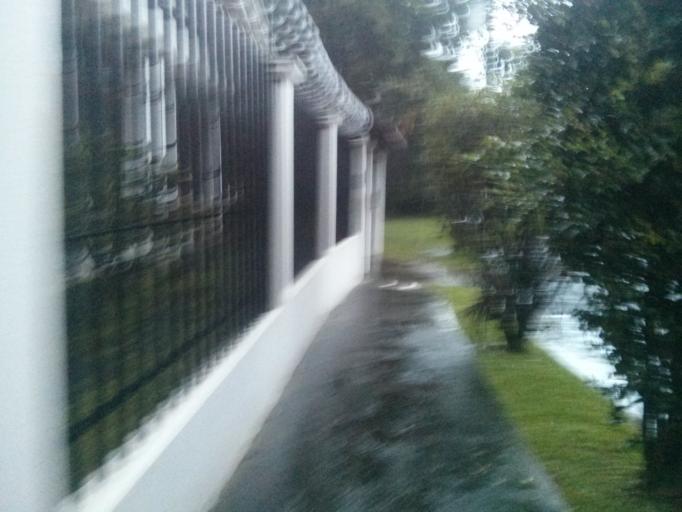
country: CR
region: San Jose
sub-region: Canton de Goicoechea
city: Guadalupe
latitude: 9.9371
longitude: -84.0586
